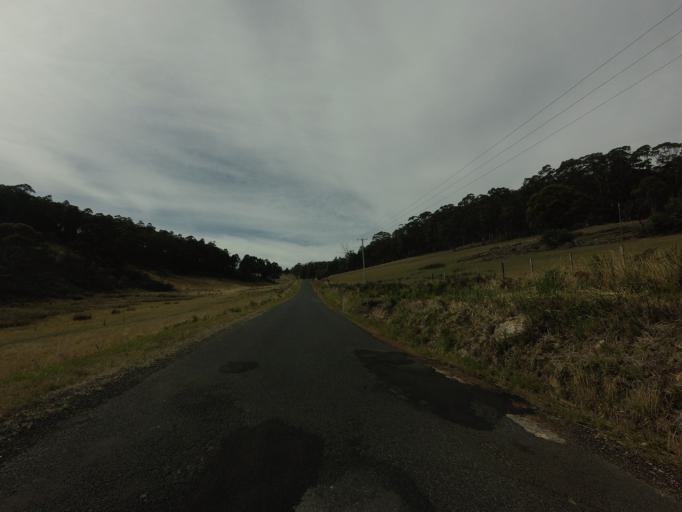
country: AU
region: Tasmania
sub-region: Sorell
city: Sorell
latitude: -42.4412
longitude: 147.5363
